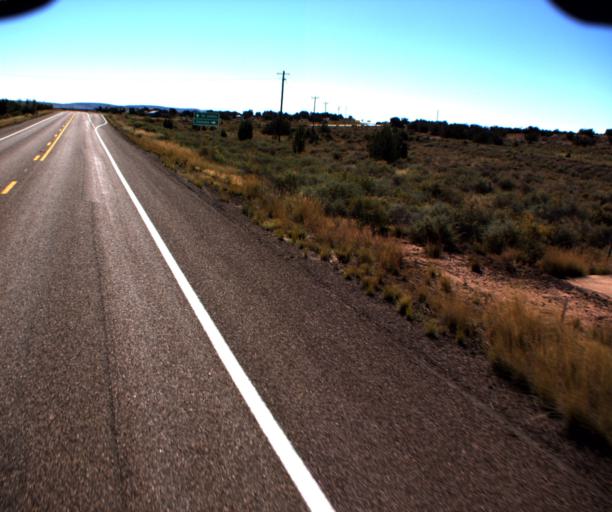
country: US
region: Arizona
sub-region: Apache County
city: Saint Johns
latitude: 34.6211
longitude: -109.6640
